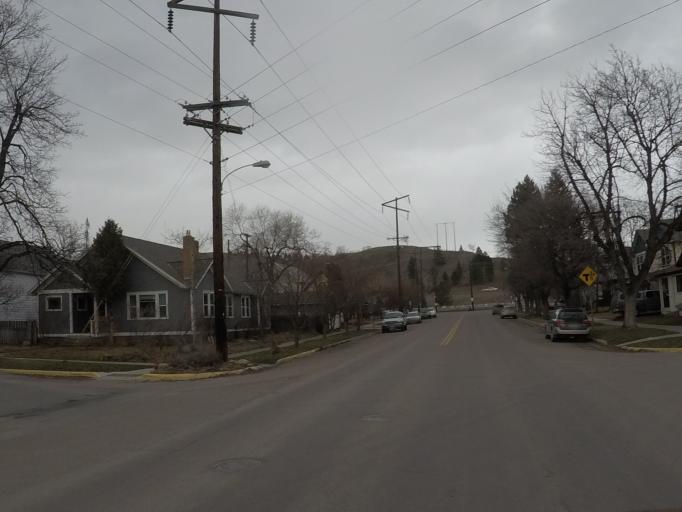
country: US
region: Montana
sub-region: Missoula County
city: Missoula
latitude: 46.8709
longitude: -113.9864
